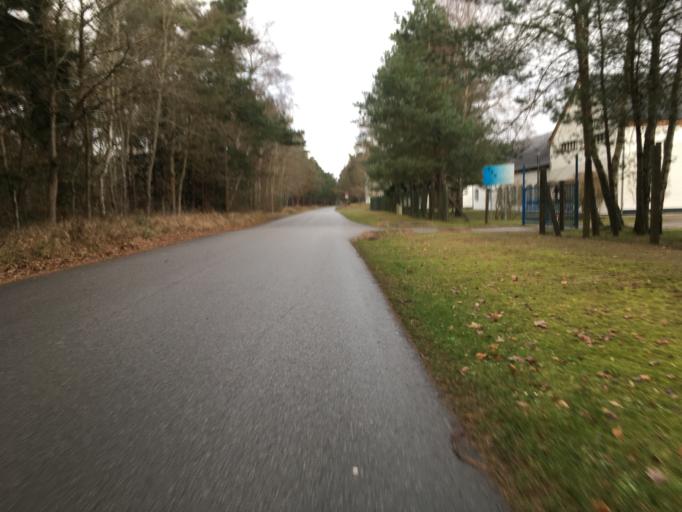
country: DE
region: Mecklenburg-Vorpommern
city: Ostseebad Binz
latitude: 54.4497
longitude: 13.5652
